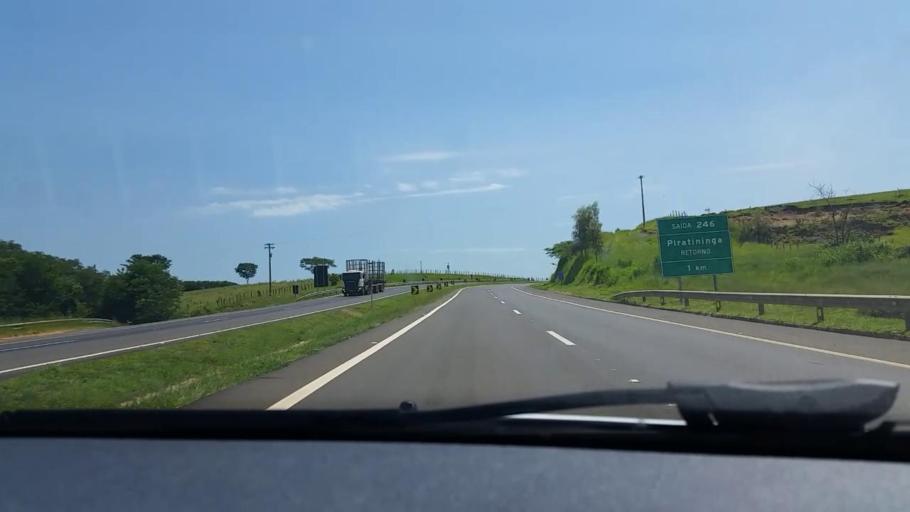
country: BR
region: Sao Paulo
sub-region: Bauru
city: Bauru
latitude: -22.4299
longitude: -49.1320
